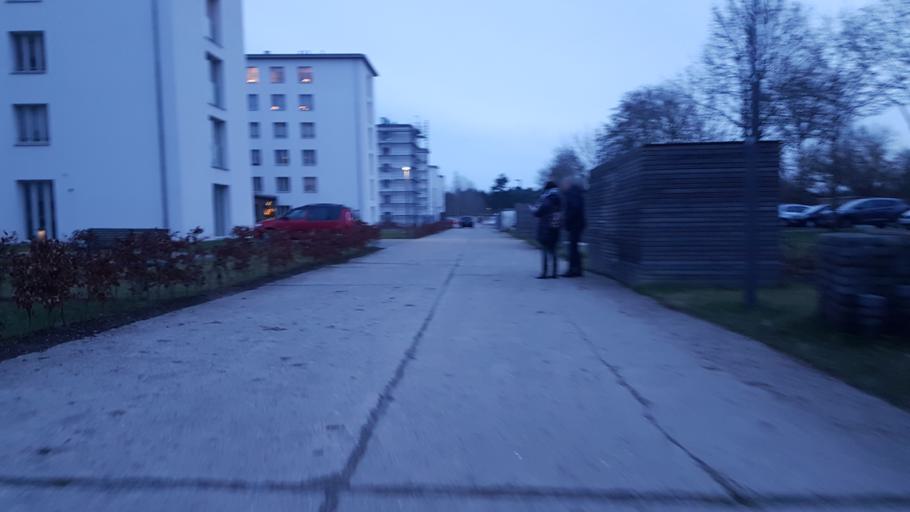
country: DE
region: Mecklenburg-Vorpommern
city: Ostseebad Binz
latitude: 54.4455
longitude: 13.5716
